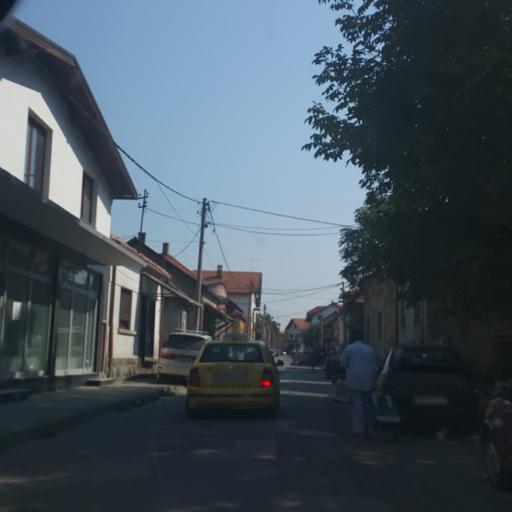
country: RS
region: Central Serbia
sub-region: Zajecarski Okrug
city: Zajecar
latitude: 43.9051
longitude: 22.2794
